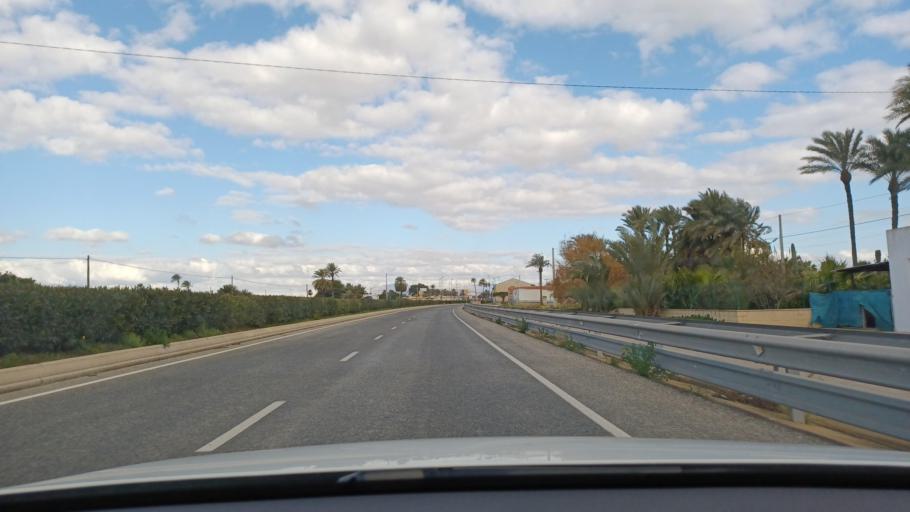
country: ES
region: Valencia
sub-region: Provincia de Alicante
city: Elche
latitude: 38.1918
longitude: -0.7009
